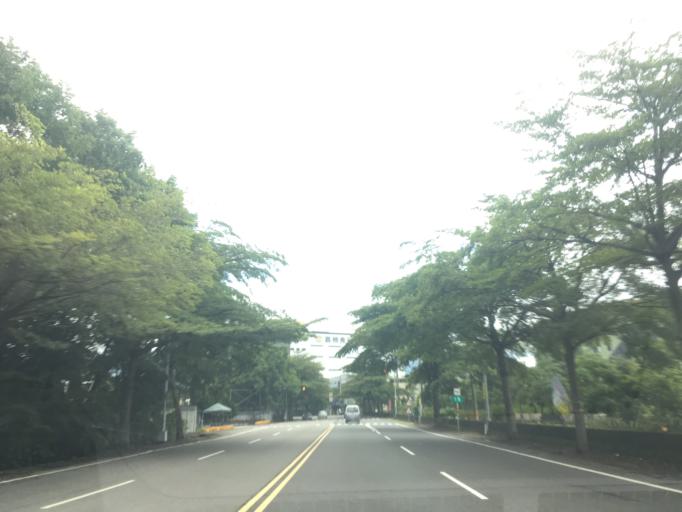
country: TW
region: Taiwan
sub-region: Yunlin
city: Douliu
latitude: 23.5934
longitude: 120.5280
